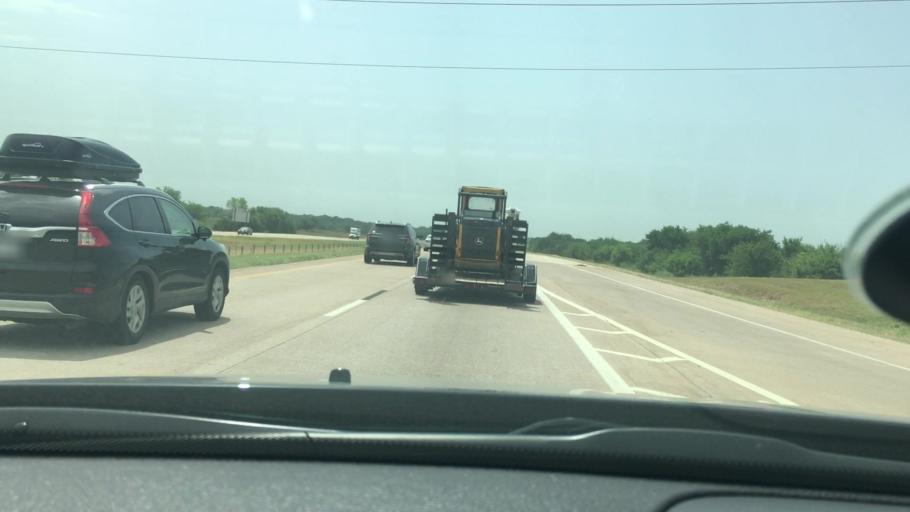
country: US
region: Oklahoma
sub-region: Garvin County
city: Pauls Valley
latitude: 34.7032
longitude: -97.2430
